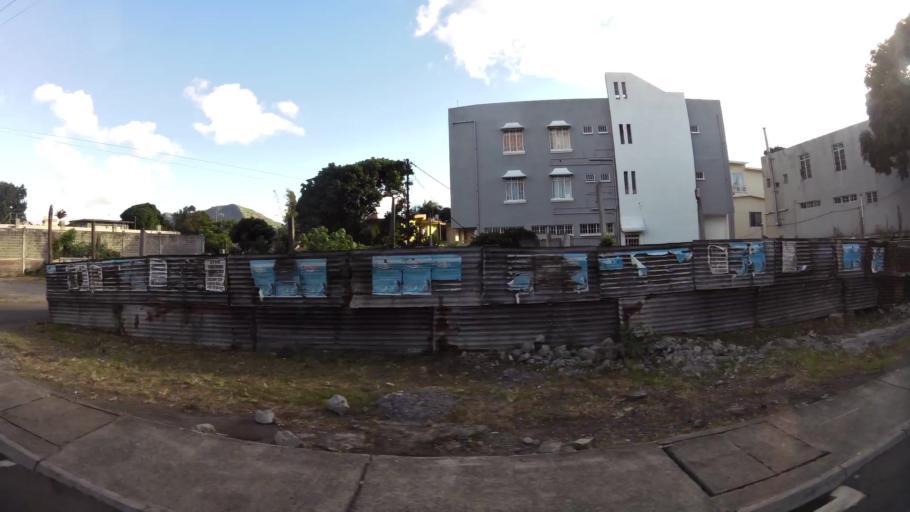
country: MU
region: Plaines Wilhems
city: Ebene
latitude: -20.2316
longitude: 57.4684
